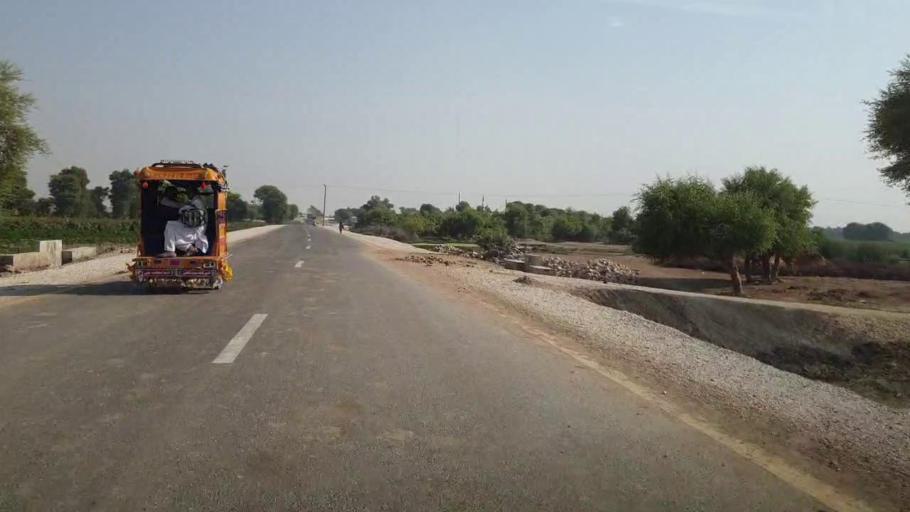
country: PK
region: Sindh
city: Bhan
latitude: 26.5653
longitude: 67.7704
